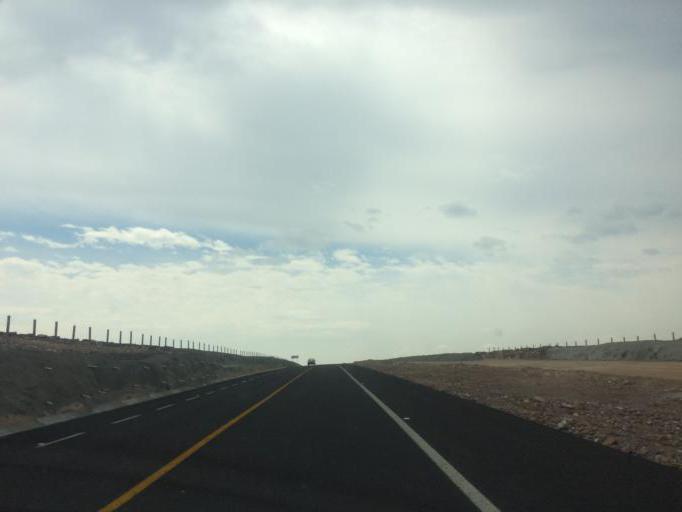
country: MX
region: Guanajuato
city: Duarte
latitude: 21.0667
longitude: -101.5371
